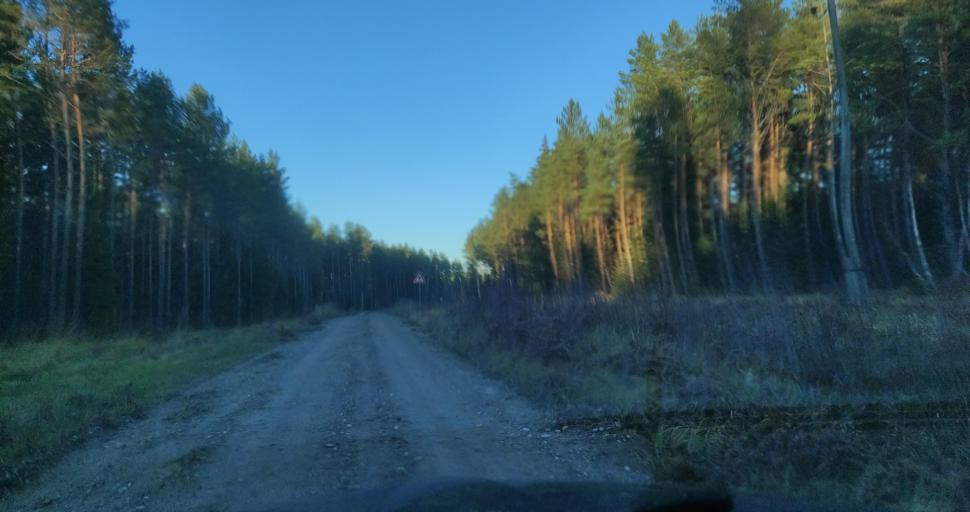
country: LV
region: Dundaga
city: Dundaga
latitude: 57.3744
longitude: 22.0787
